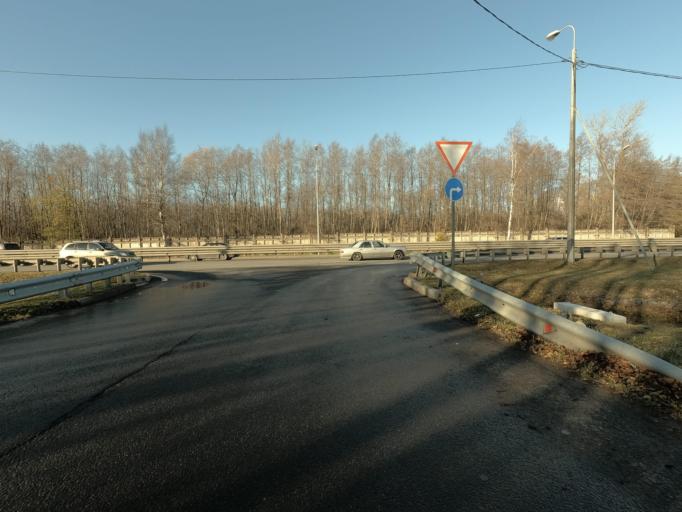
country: RU
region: St.-Petersburg
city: Krasnogvargeisky
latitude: 59.9869
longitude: 30.5221
